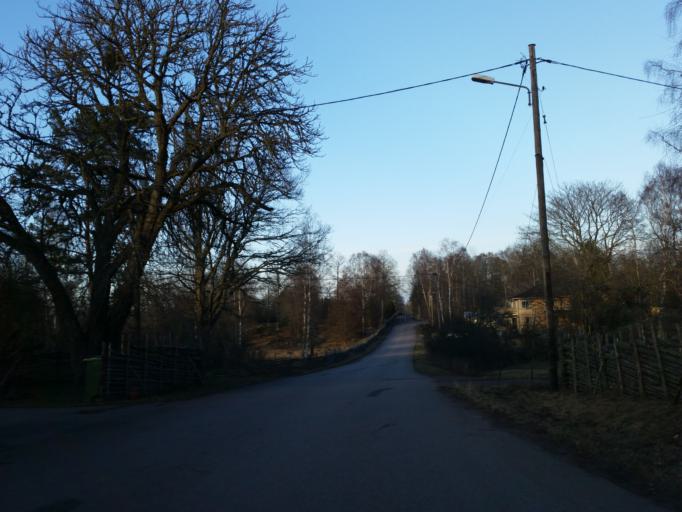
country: SE
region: Kalmar
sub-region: Oskarshamns Kommun
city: Oskarshamn
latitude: 57.3345
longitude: 16.4763
